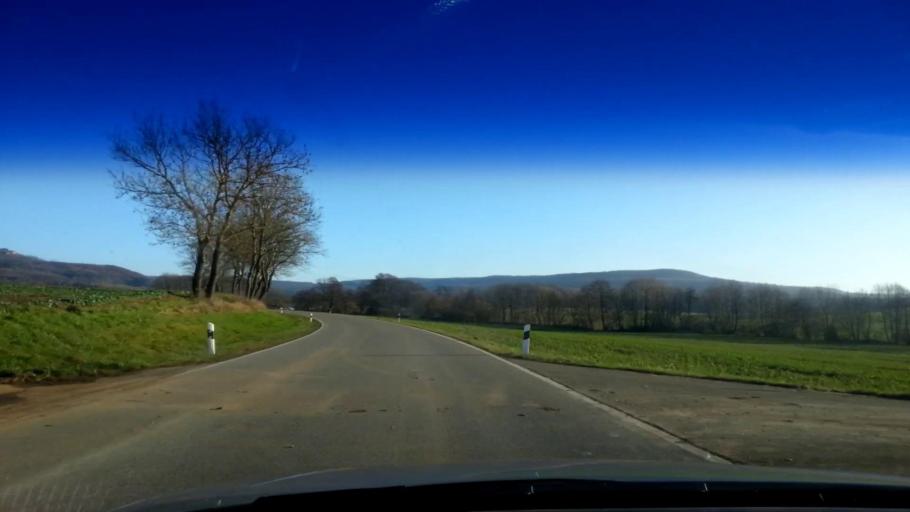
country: DE
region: Bavaria
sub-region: Upper Franconia
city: Schesslitz
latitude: 49.9566
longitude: 11.0104
